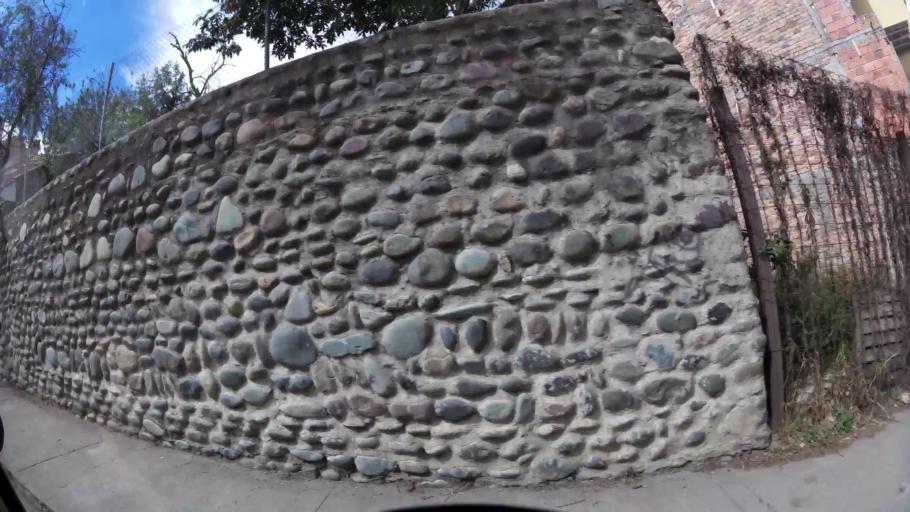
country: EC
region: Azuay
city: Cuenca
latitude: -2.8818
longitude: -78.9782
